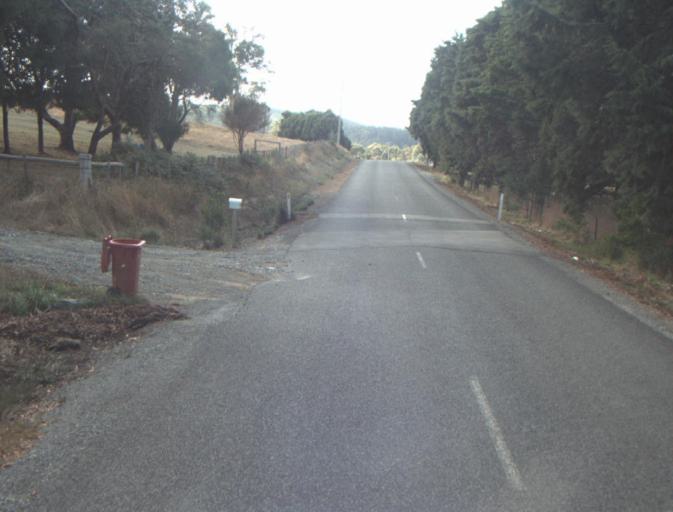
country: AU
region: Tasmania
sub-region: Launceston
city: Mayfield
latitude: -41.2164
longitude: 147.1364
